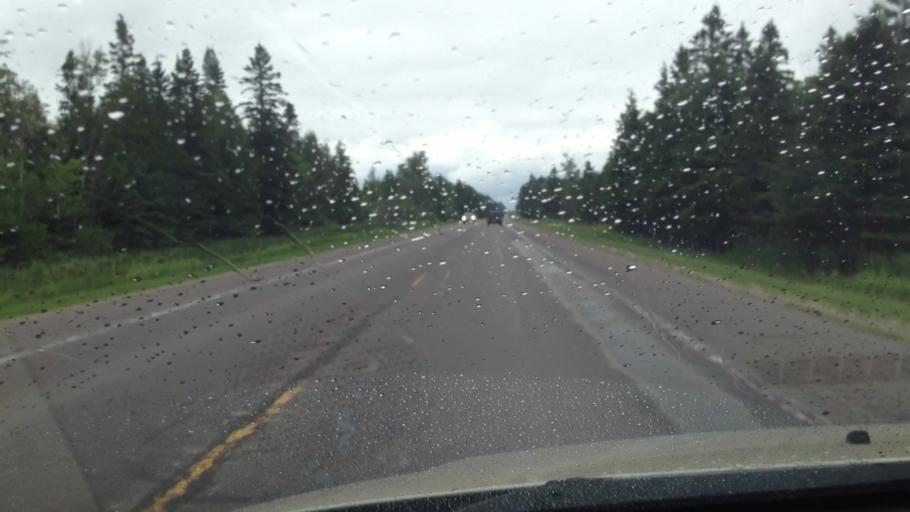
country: US
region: Michigan
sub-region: Schoolcraft County
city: Manistique
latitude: 46.0414
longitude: -85.9726
